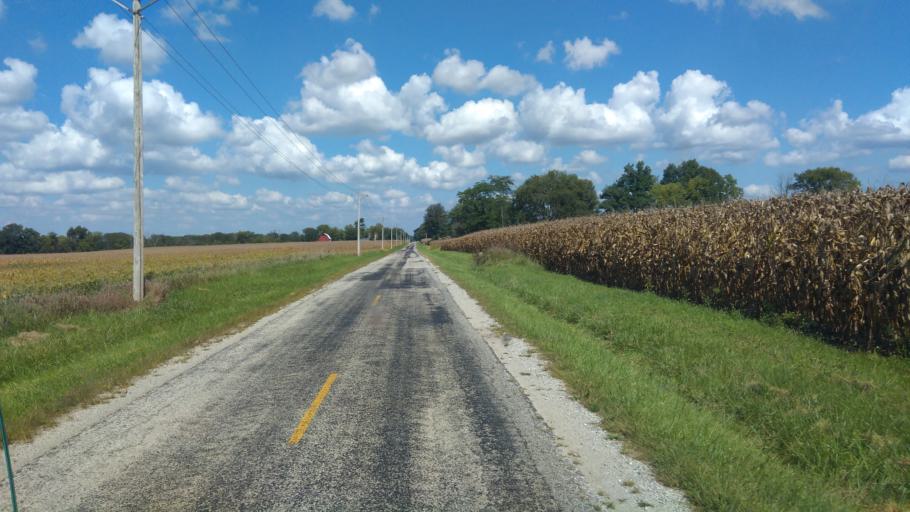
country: US
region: Ohio
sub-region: Wyandot County
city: Upper Sandusky
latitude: 40.6639
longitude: -83.3431
